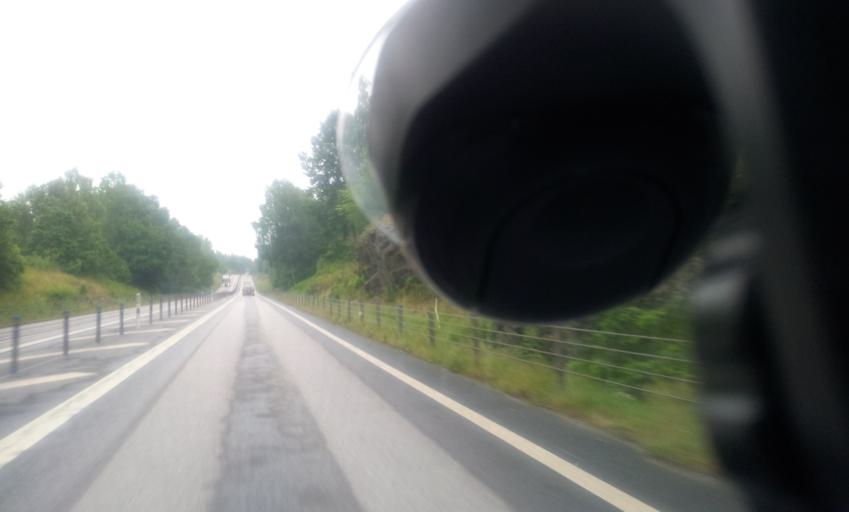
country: SE
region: Kalmar
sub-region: Vasterviks Kommun
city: Gamleby
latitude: 57.8668
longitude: 16.4174
